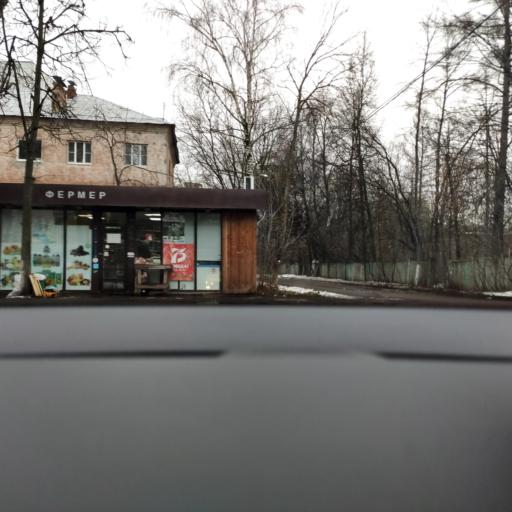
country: RU
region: Moskovskaya
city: Lesnyye Polyany
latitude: 55.9496
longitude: 37.8689
